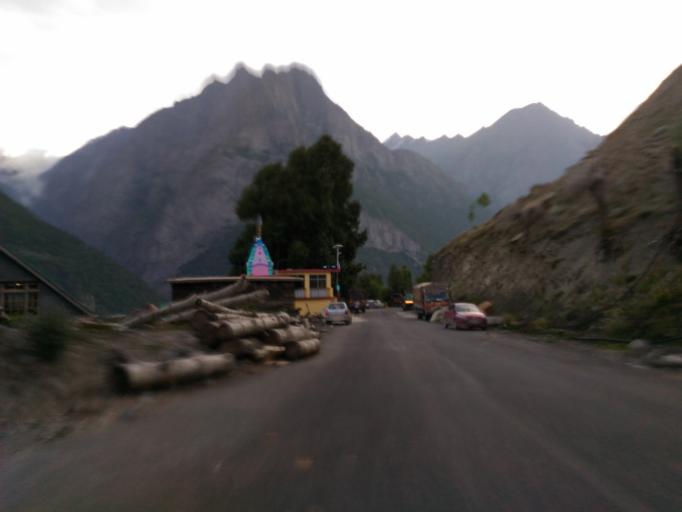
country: IN
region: Himachal Pradesh
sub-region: Lahul and Spiti
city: Kyelang
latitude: 32.5139
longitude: 77.0142
